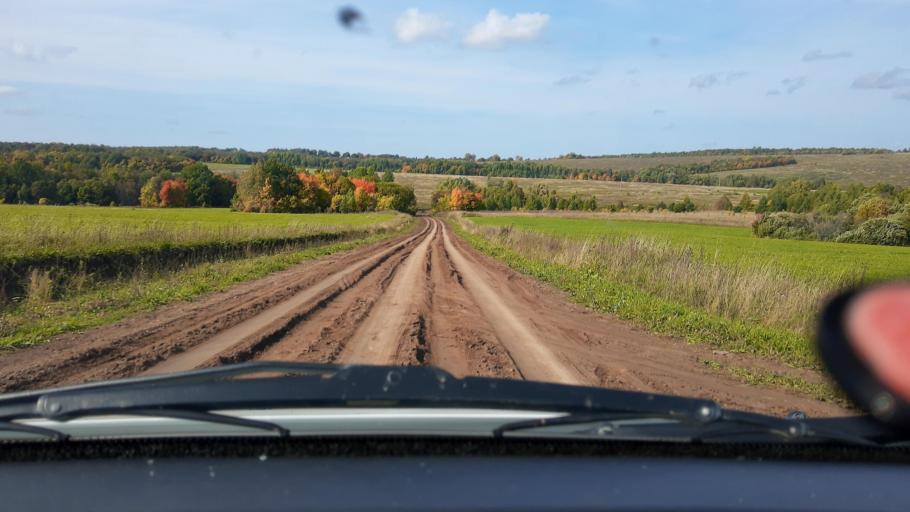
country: RU
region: Bashkortostan
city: Kudeyevskiy
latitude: 54.7134
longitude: 56.6386
